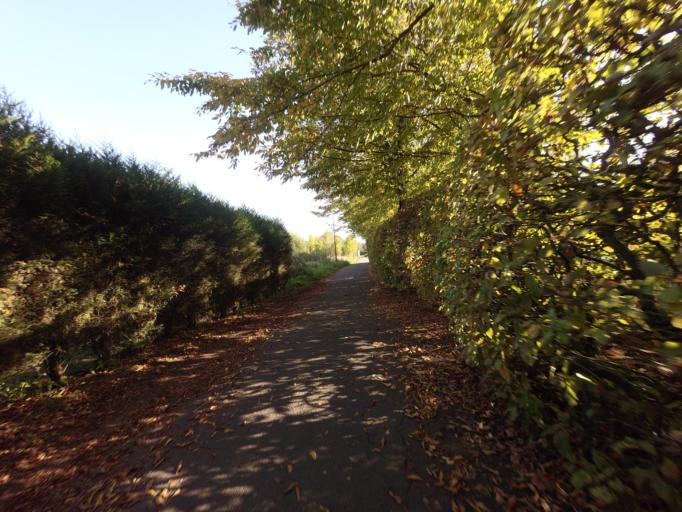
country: BE
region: Flanders
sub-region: Provincie Antwerpen
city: Lint
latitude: 51.1259
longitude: 4.5010
